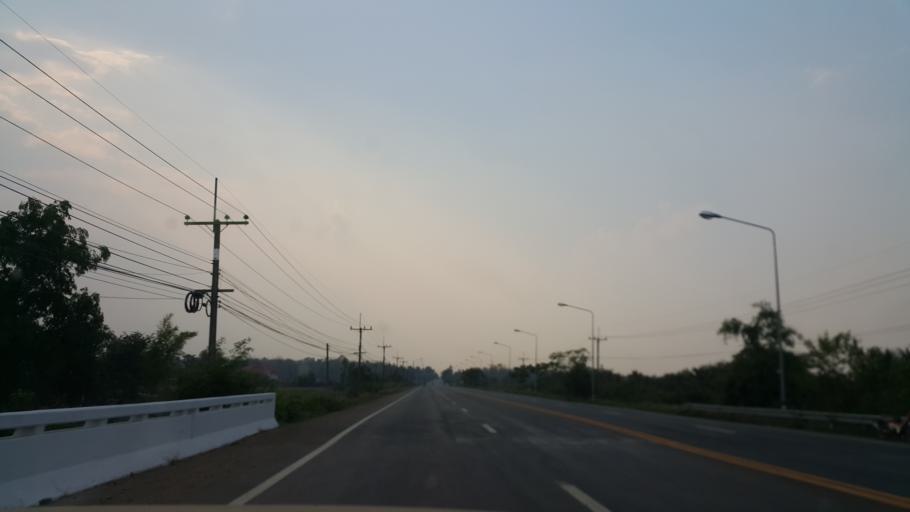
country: TH
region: Nakhon Phanom
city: Renu Nakhon
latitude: 17.0232
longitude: 104.7187
